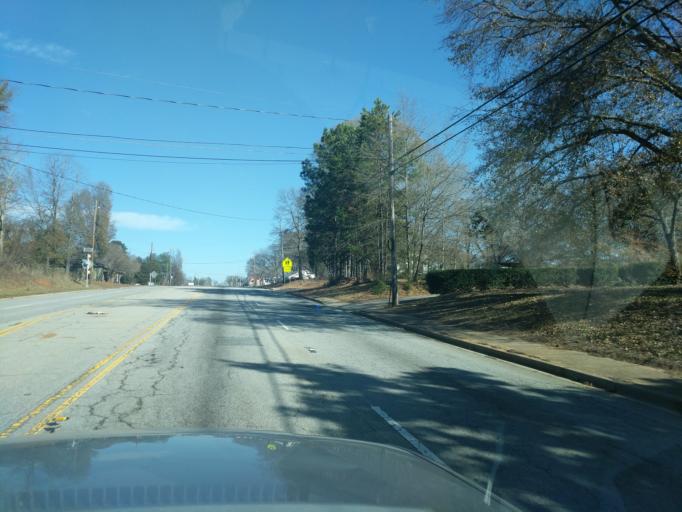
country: US
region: South Carolina
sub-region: Spartanburg County
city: Mayo
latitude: 35.0829
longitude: -81.8609
